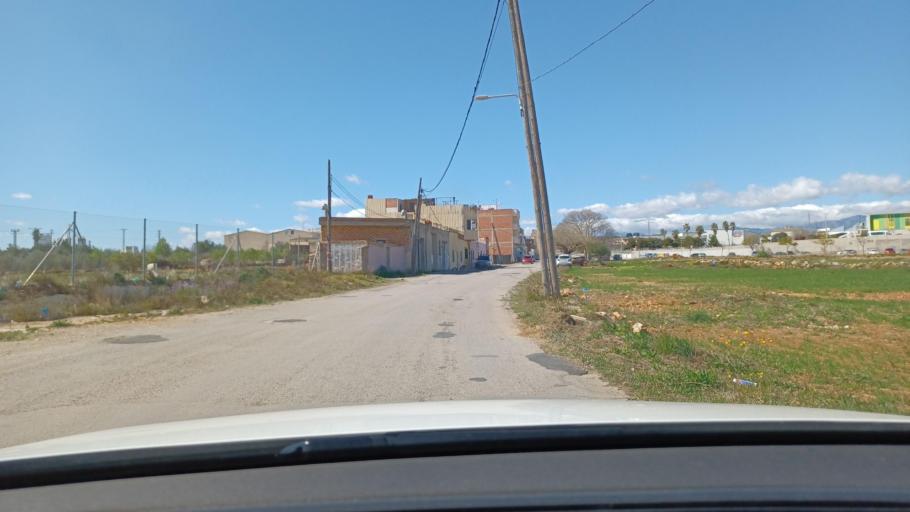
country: ES
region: Catalonia
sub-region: Provincia de Tarragona
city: Amposta
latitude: 40.7006
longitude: 0.5712
